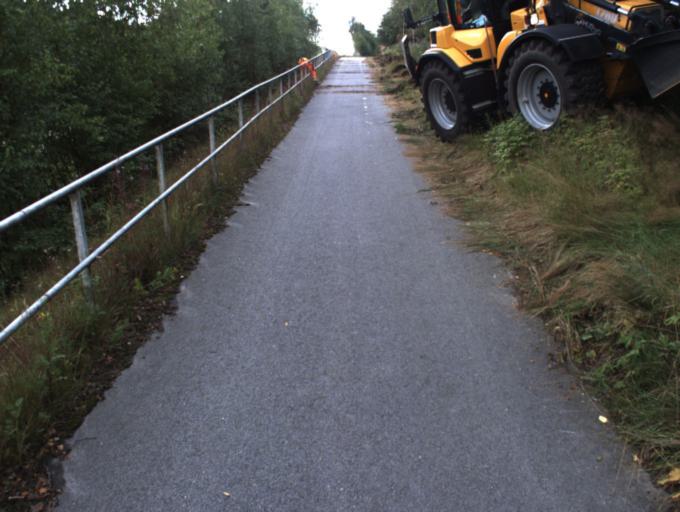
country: SE
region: Skane
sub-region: Helsingborg
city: Odakra
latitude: 56.0823
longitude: 12.7215
